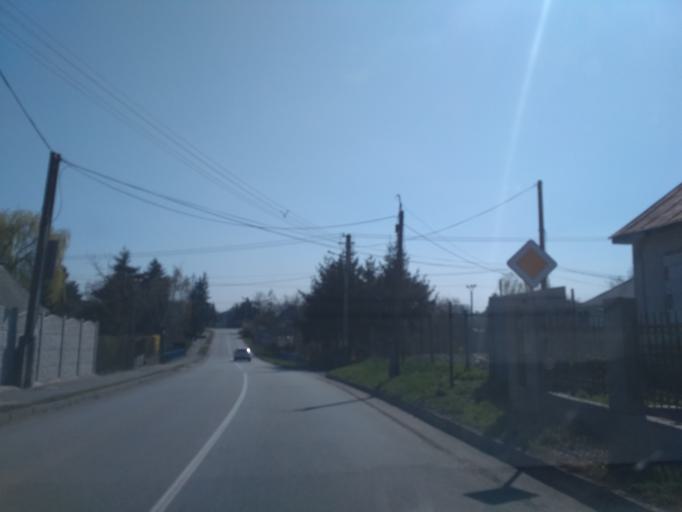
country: SK
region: Kosicky
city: Secovce
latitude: 48.7021
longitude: 21.6471
